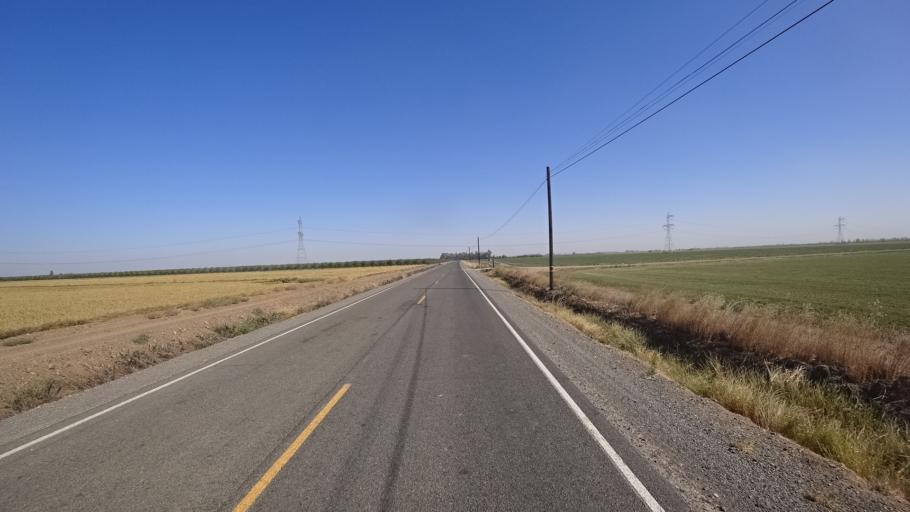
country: US
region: California
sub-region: Yolo County
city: Winters
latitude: 38.5837
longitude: -121.9180
